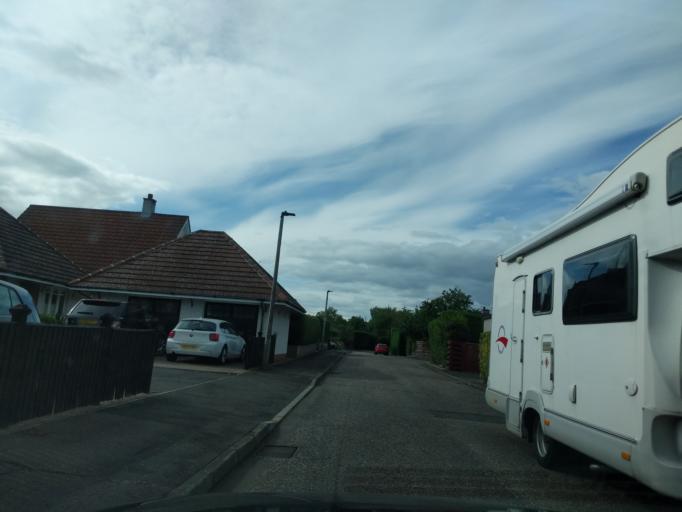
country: GB
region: Scotland
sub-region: Edinburgh
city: Colinton
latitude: 55.9584
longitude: -3.2695
